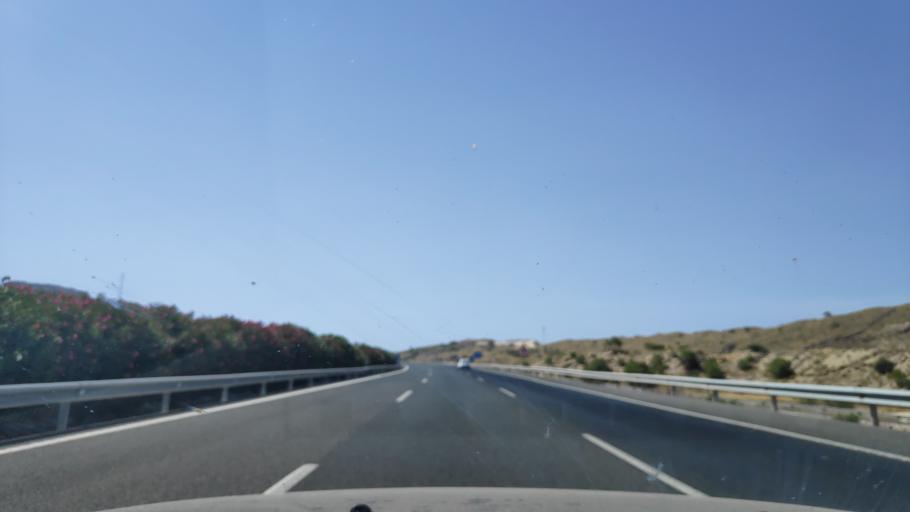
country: ES
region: Murcia
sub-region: Murcia
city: Ulea
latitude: 38.1595
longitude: -1.2990
